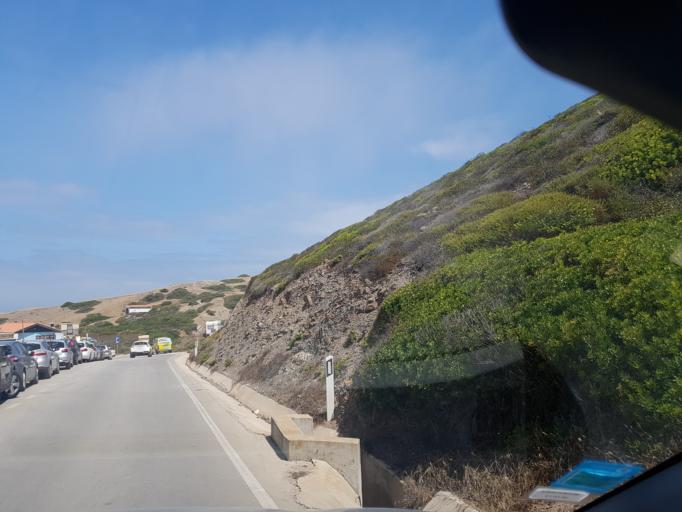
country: PT
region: Faro
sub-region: Vila do Bispo
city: Vila do Bispo
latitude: 37.1086
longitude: -8.9352
